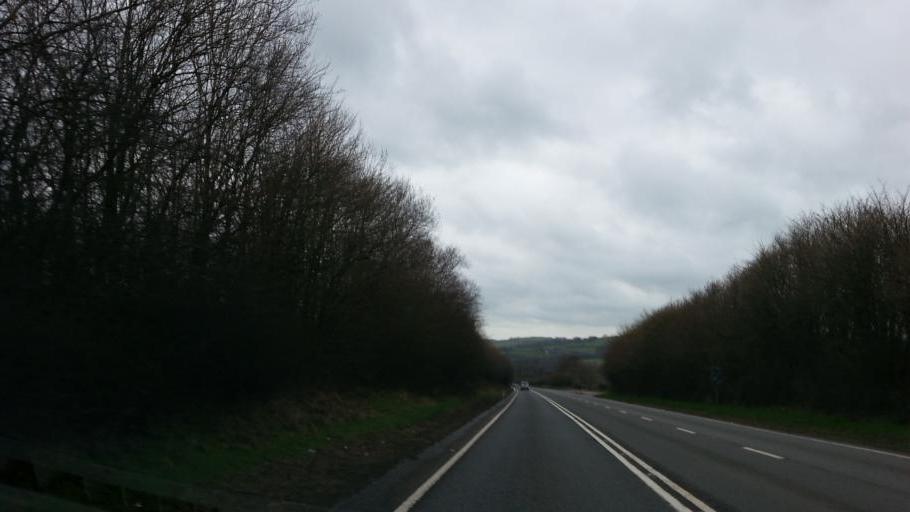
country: GB
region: England
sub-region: Devon
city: South Molton
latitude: 51.0236
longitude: -3.8089
